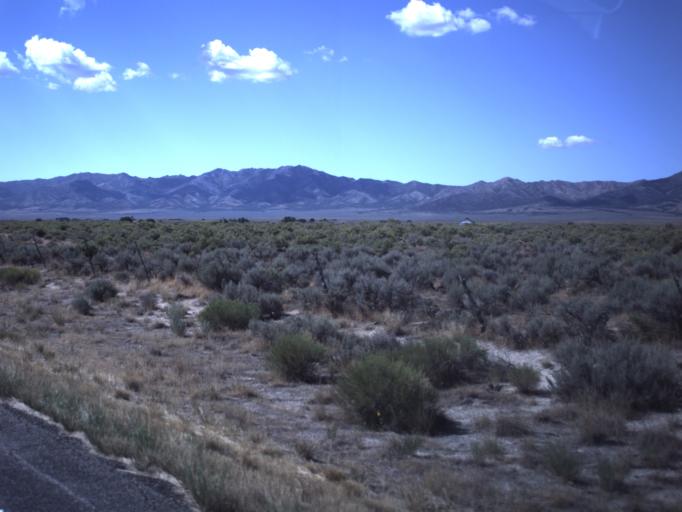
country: US
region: Utah
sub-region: Tooele County
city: Tooele
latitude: 40.1187
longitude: -112.4308
